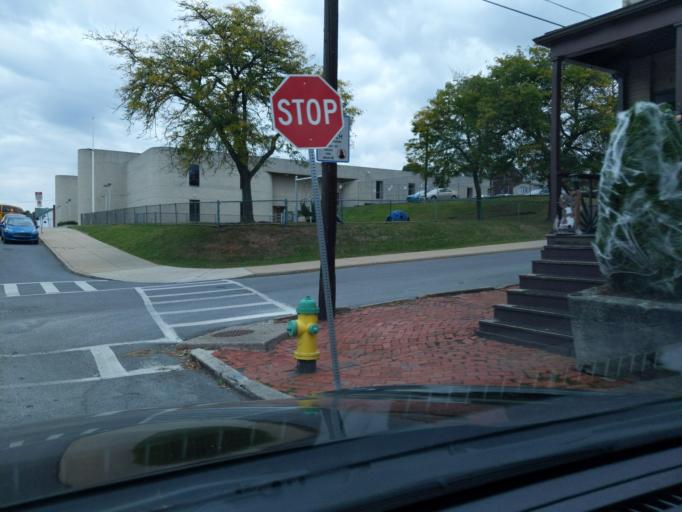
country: US
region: Pennsylvania
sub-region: Blair County
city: Altoona
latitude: 40.5166
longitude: -78.3871
